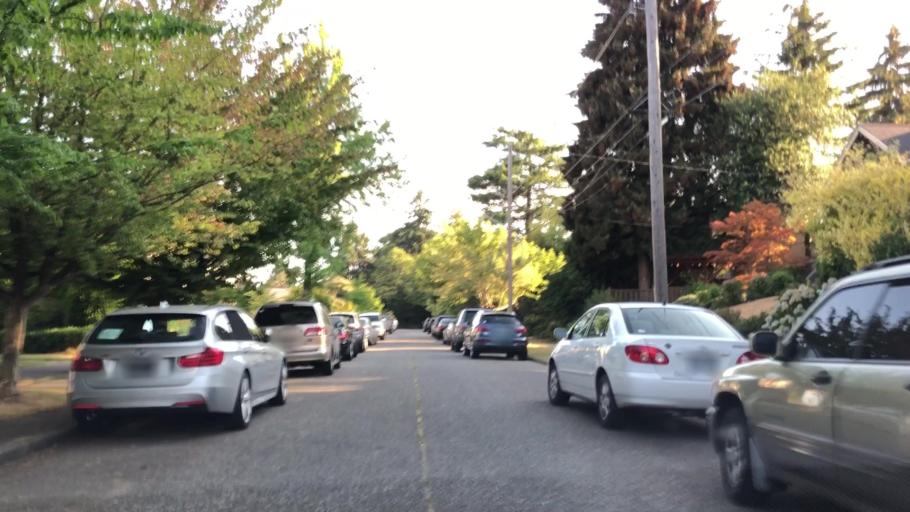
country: US
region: Washington
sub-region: King County
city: Yarrow Point
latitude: 47.6635
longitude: -122.2794
